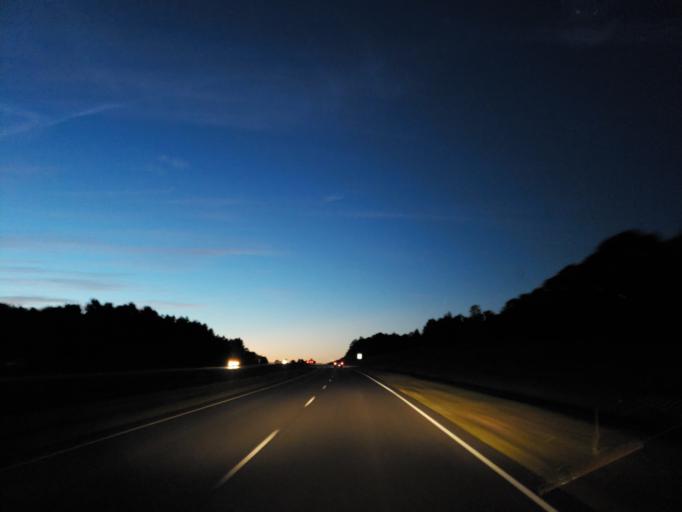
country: US
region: Mississippi
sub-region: Clarke County
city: Quitman
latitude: 32.1028
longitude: -88.7078
